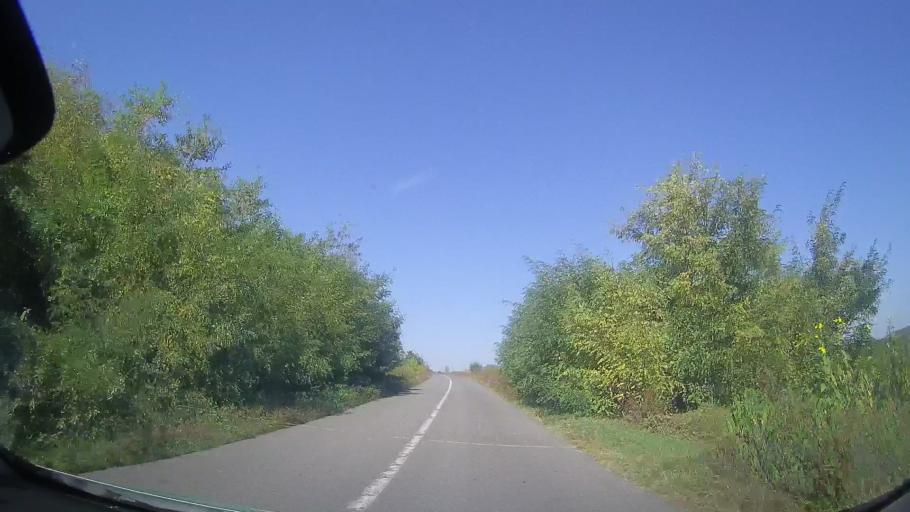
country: RO
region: Timis
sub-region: Comuna Balint
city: Balint
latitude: 45.8203
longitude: 21.8525
